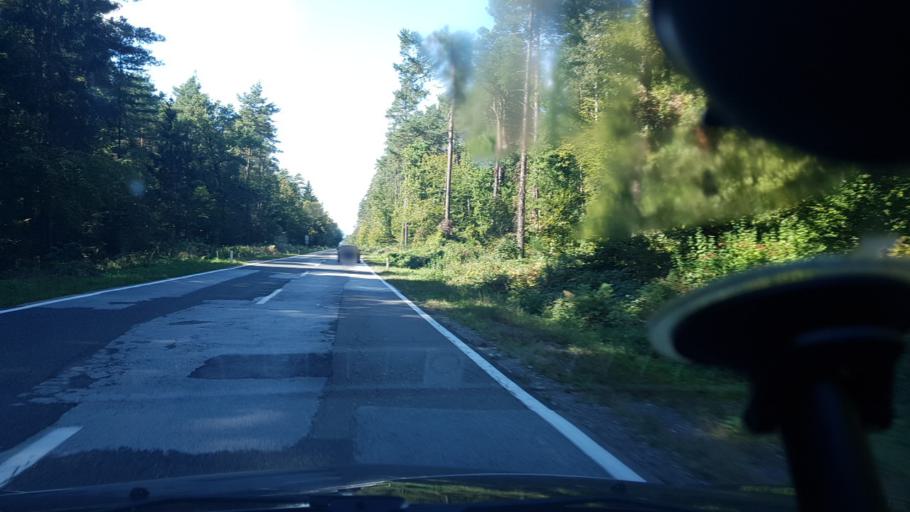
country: SI
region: Kidricevo
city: Kidricevo
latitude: 46.4109
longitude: 15.7817
